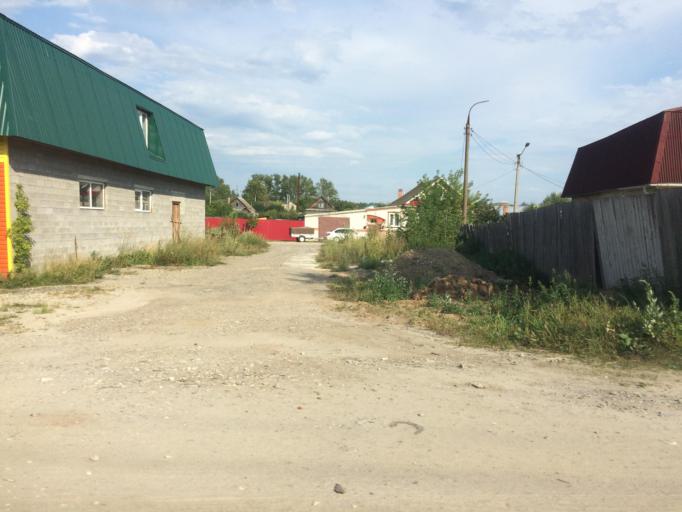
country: RU
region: Mariy-El
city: Yoshkar-Ola
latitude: 56.5485
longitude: 47.9830
